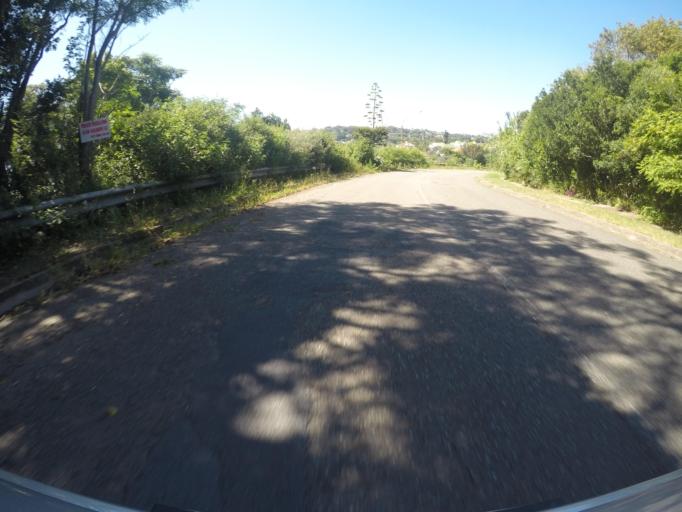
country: ZA
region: Eastern Cape
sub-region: Buffalo City Metropolitan Municipality
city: East London
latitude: -32.9710
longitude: 27.9210
